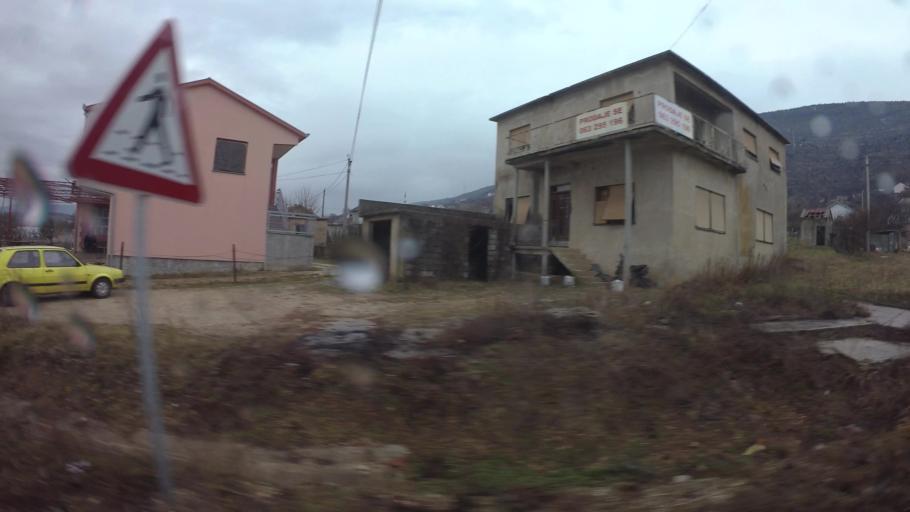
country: BA
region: Federation of Bosnia and Herzegovina
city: Blagaj
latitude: 43.2900
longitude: 17.8588
